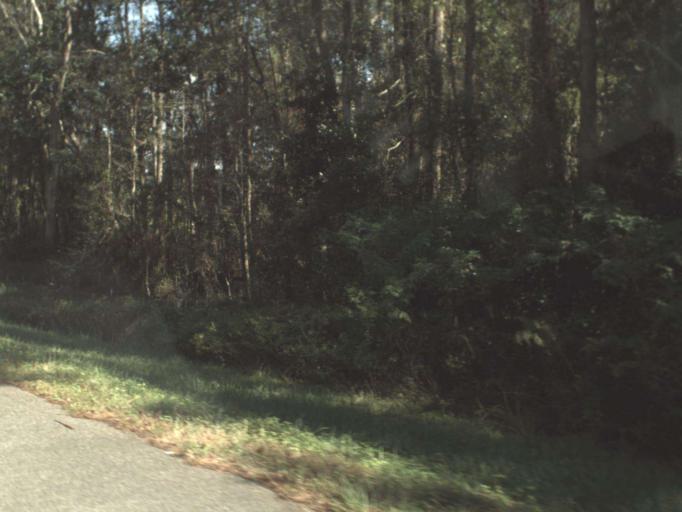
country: US
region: Alabama
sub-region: Geneva County
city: Samson
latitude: 30.9789
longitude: -86.1345
